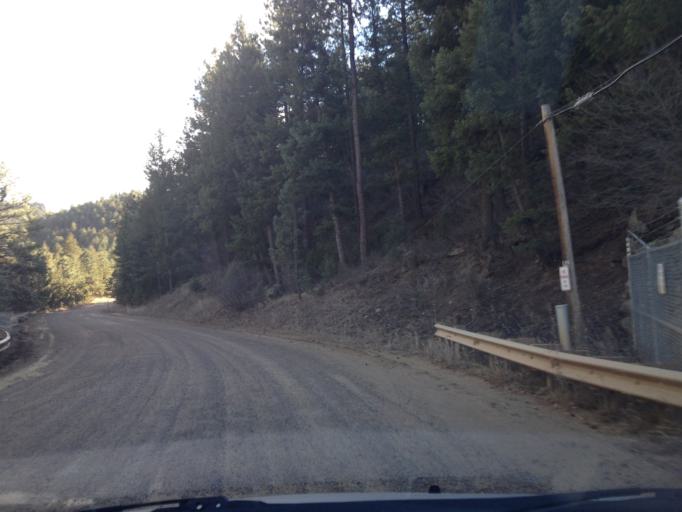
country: US
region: Colorado
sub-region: Boulder County
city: Coal Creek
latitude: 39.9393
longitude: -105.3501
